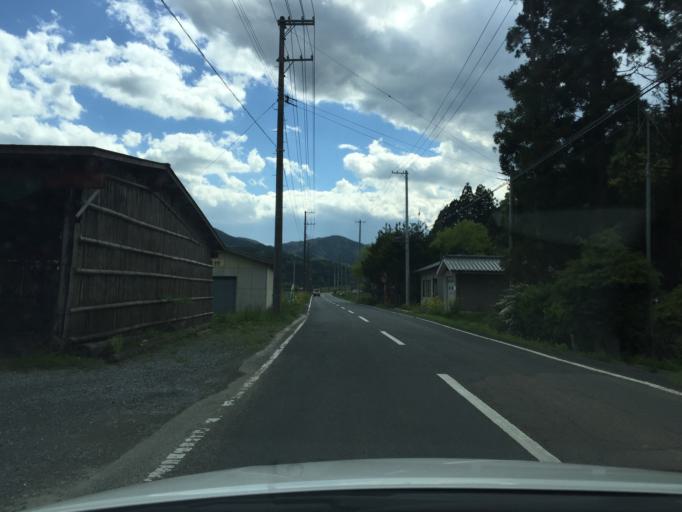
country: JP
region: Miyagi
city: Marumori
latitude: 37.7272
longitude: 140.8938
